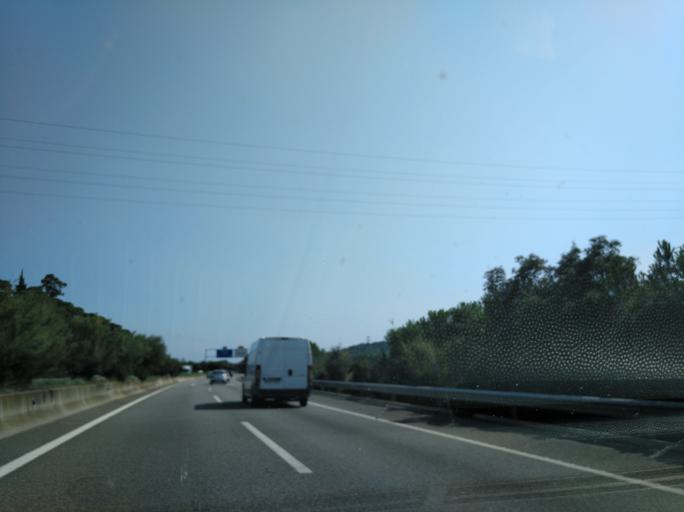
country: ES
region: Catalonia
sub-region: Provincia de Barcelona
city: Argentona
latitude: 41.5560
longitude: 2.4084
